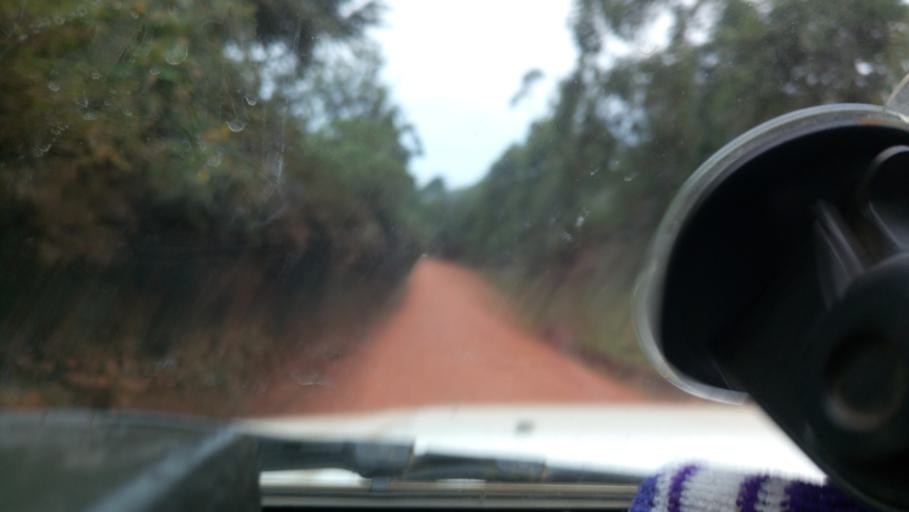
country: KE
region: Kericho
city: Litein
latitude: -0.6049
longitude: 35.2264
